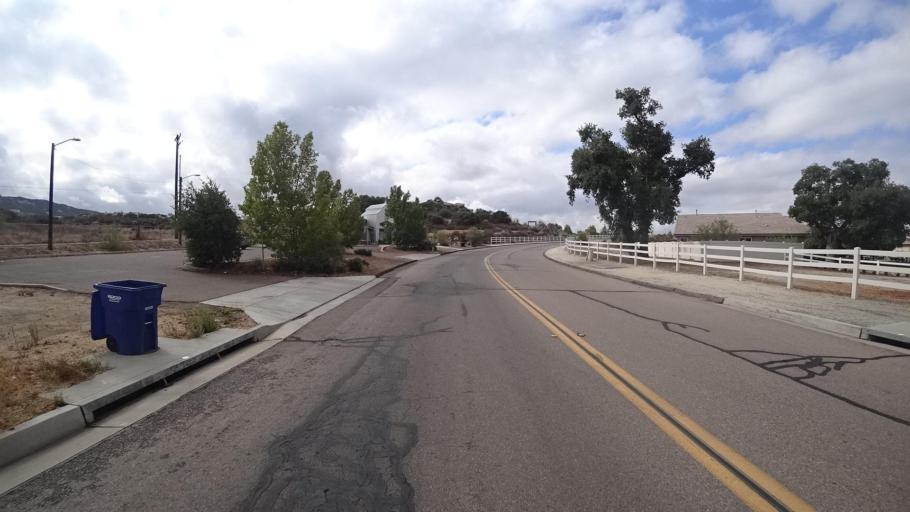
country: US
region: California
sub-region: San Diego County
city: Campo
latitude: 32.6217
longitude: -116.4634
